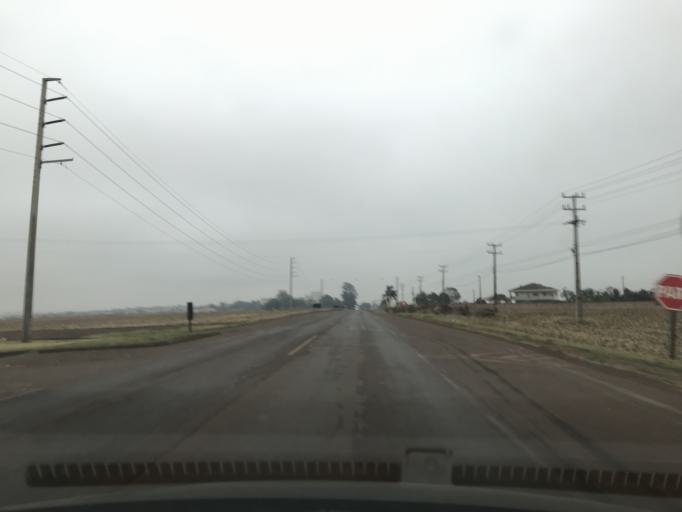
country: BR
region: Parana
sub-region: Palotina
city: Palotina
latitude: -24.3162
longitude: -53.8332
